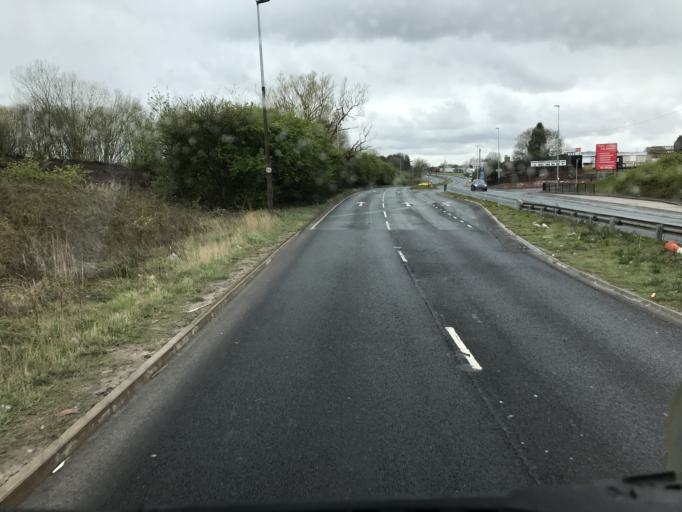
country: GB
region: England
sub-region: Trafford
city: Carrington
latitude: 53.4692
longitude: -2.3858
